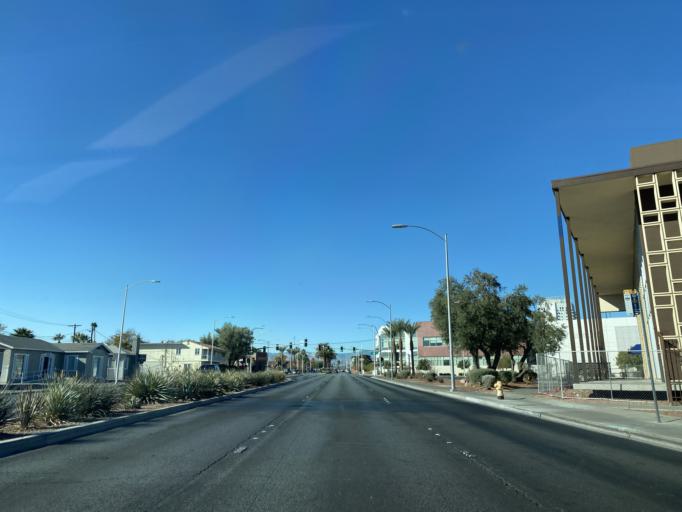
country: US
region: Nevada
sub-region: Clark County
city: Las Vegas
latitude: 36.1589
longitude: -115.1416
